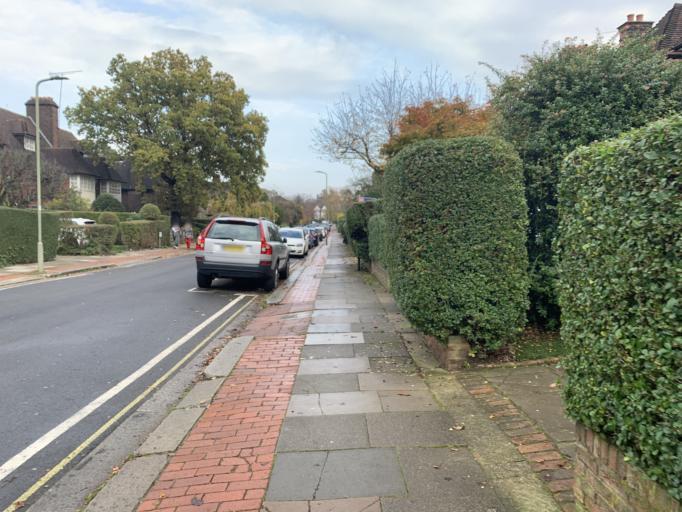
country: GB
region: England
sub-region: Greater London
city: Belsize Park
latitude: 51.5737
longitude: -0.1944
